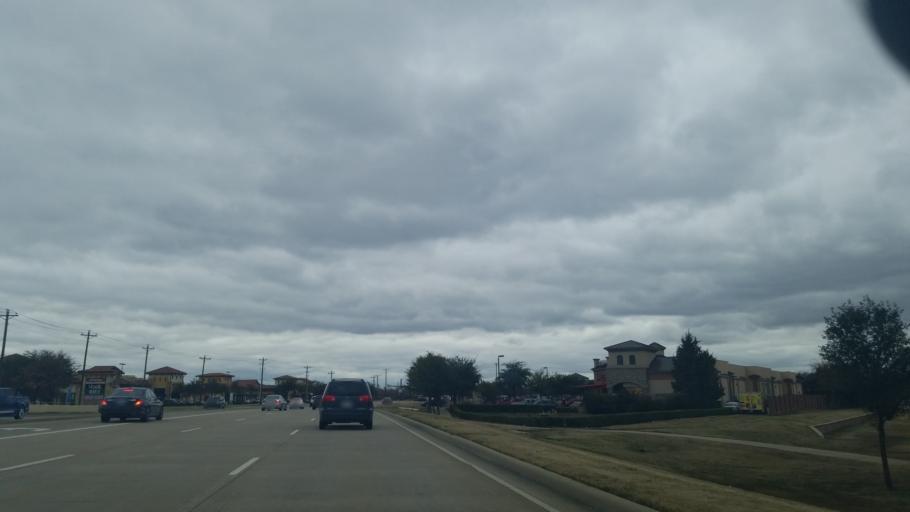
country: US
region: Texas
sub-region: Denton County
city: Double Oak
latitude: 33.0640
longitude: -97.0789
